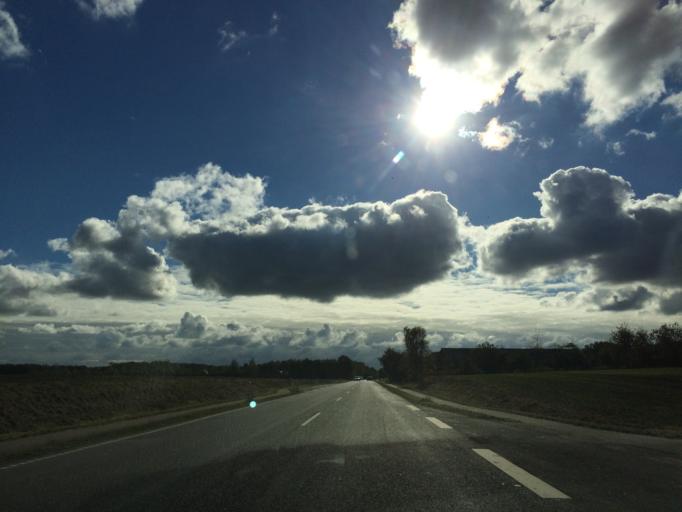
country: DK
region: Central Jutland
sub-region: Skanderborg Kommune
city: Ry
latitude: 56.1242
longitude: 9.7914
